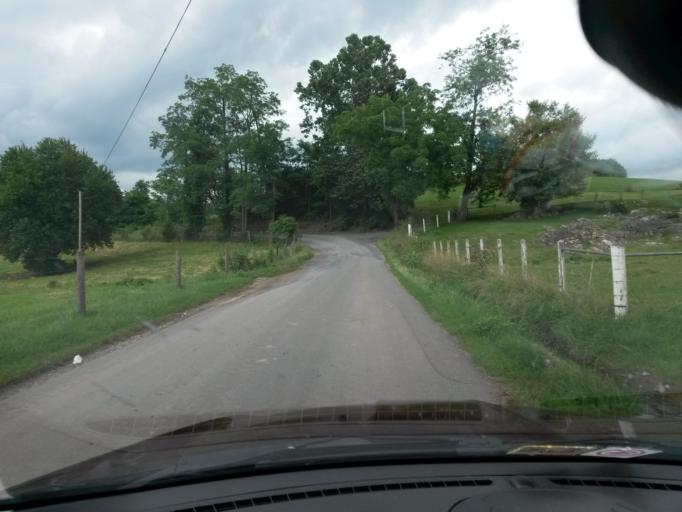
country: US
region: Virginia
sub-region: Rockingham County
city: Dayton
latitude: 38.4620
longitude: -78.9743
